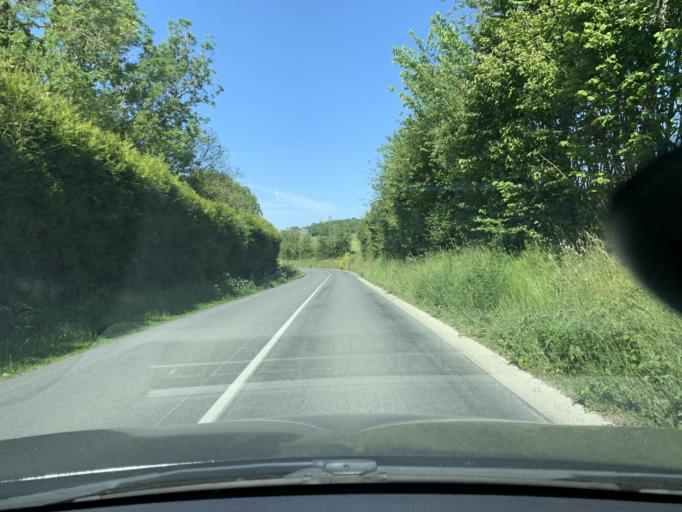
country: FR
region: Nord-Pas-de-Calais
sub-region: Departement du Nord
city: Masnieres
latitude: 50.0780
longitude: 3.2141
